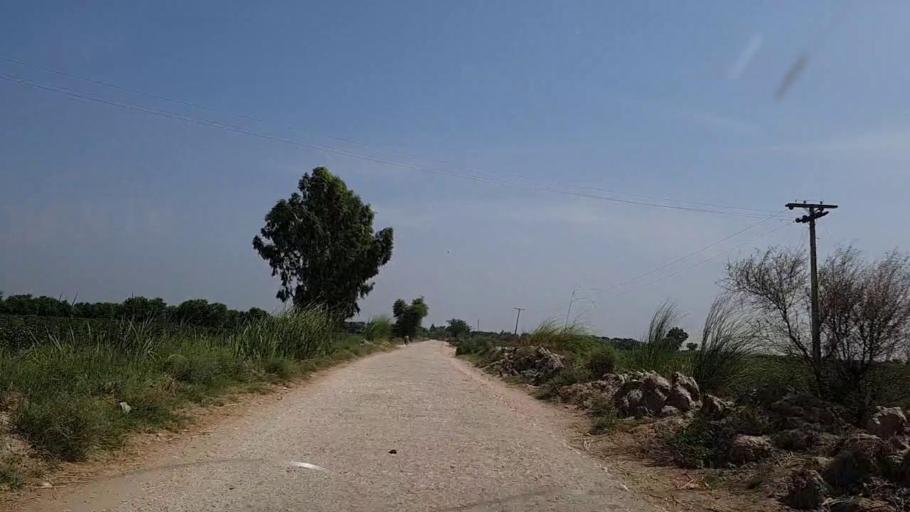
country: PK
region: Sindh
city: Khanpur
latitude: 27.7901
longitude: 69.3177
